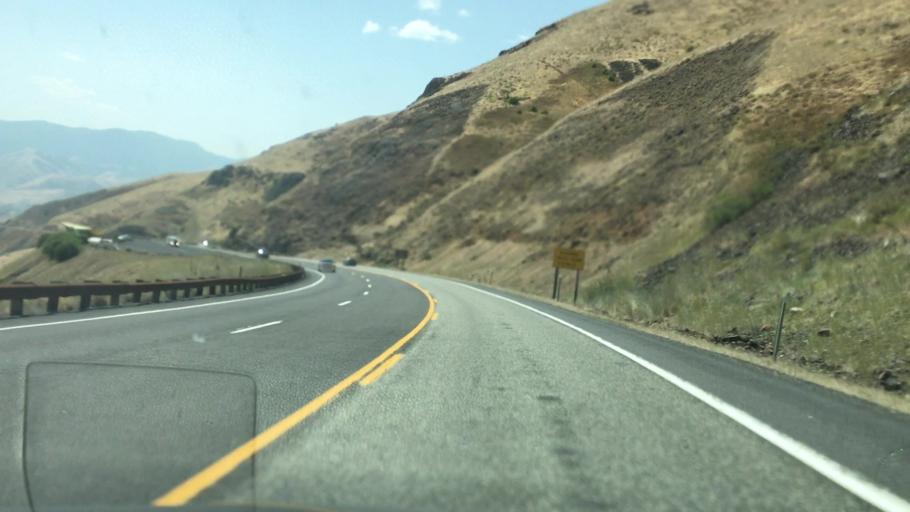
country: US
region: Idaho
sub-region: Idaho County
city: Grangeville
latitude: 45.8041
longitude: -116.2860
